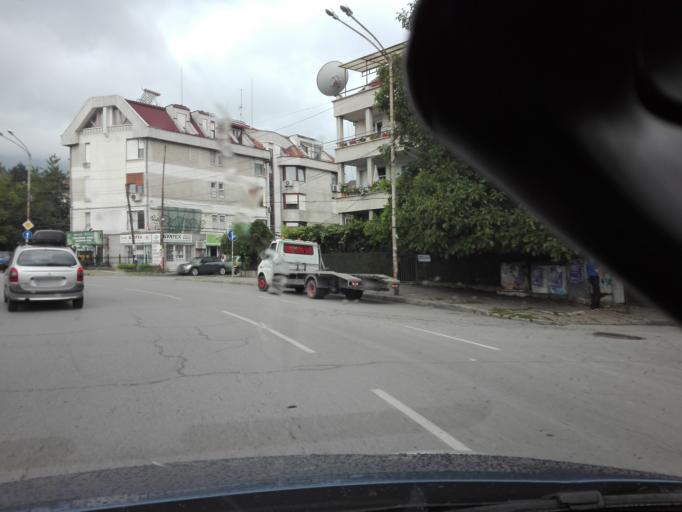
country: BG
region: Sofia-Capital
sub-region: Stolichna Obshtina
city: Sofia
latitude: 42.6644
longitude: 23.2655
